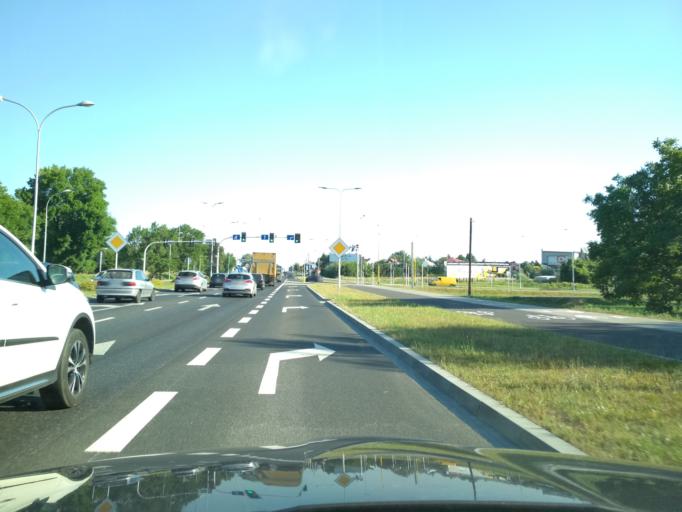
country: PL
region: Subcarpathian Voivodeship
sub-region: Rzeszow
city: Rzeszow
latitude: 50.0652
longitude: 21.9920
